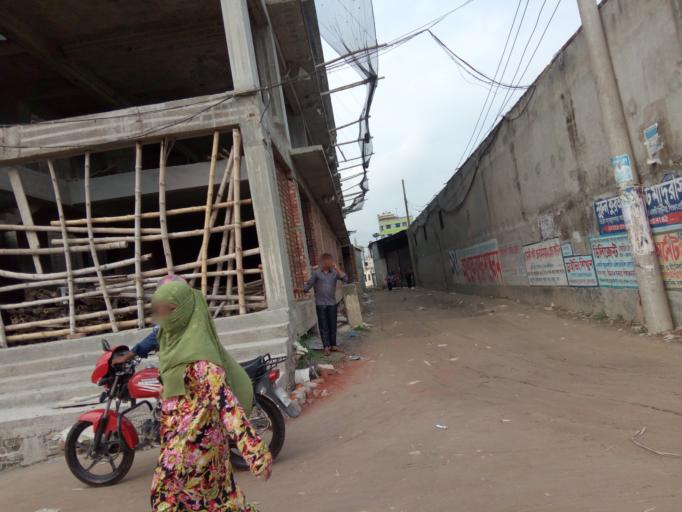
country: BD
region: Dhaka
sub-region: Dhaka
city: Dhaka
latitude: 23.7006
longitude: 90.4643
